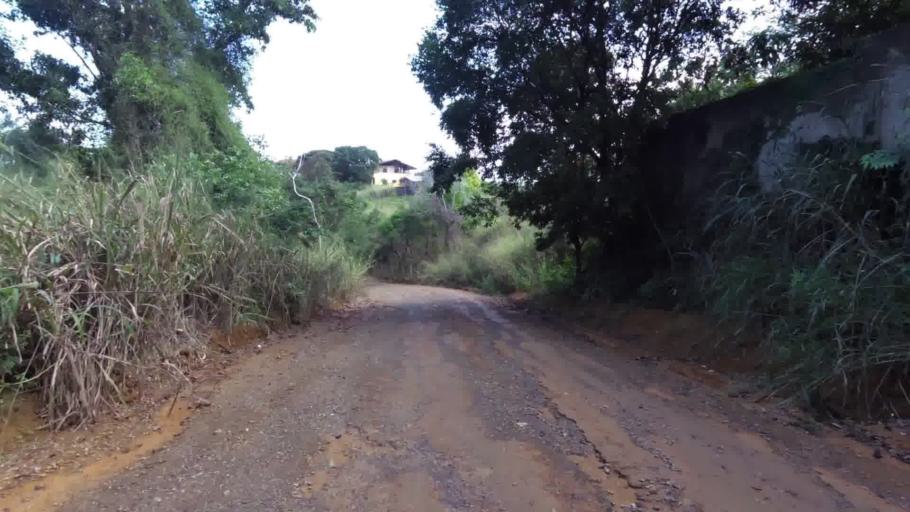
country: BR
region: Espirito Santo
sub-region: Piuma
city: Piuma
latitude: -20.8256
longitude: -40.6884
